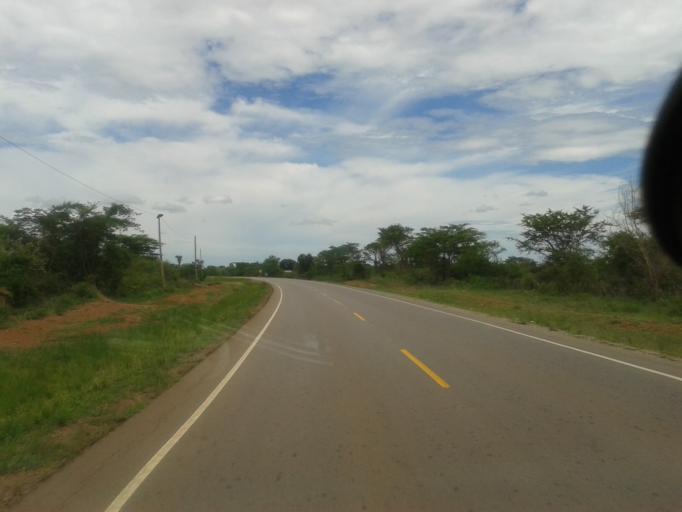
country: UG
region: Western Region
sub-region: Kiryandongo District
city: Masindi Port
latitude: 1.5603
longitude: 32.0344
